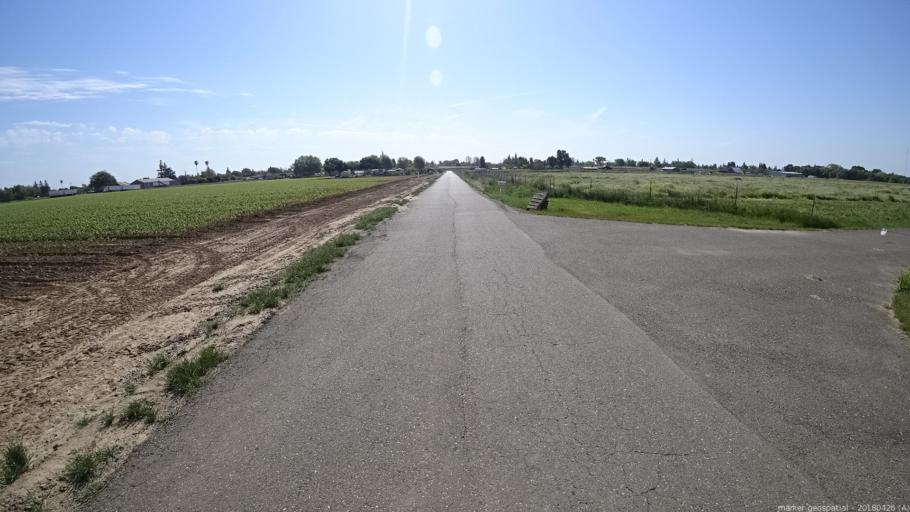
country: US
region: California
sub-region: Yolo County
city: West Sacramento
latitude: 38.5111
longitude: -121.5617
